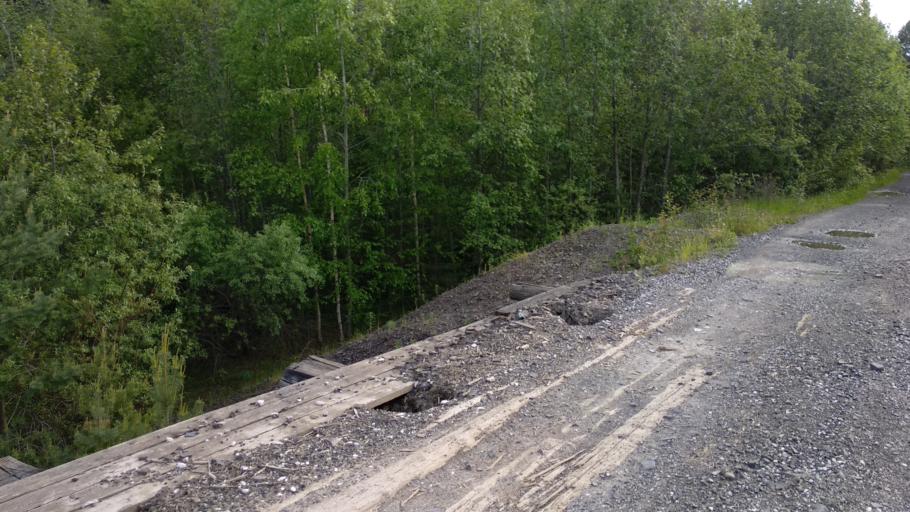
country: RU
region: Sverdlovsk
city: Karpinsk
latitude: 59.7653
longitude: 59.9148
